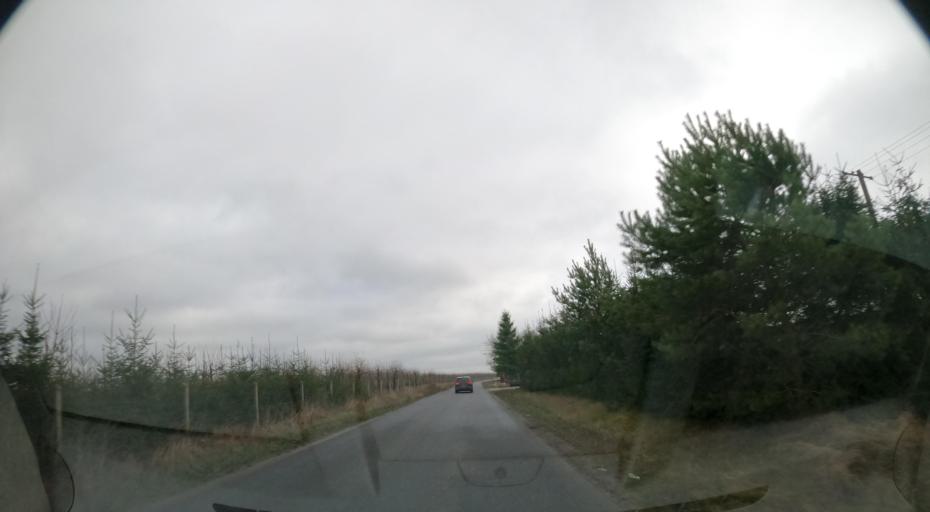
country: PL
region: Greater Poland Voivodeship
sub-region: Powiat pilski
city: Lobzenica
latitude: 53.2451
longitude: 17.2929
